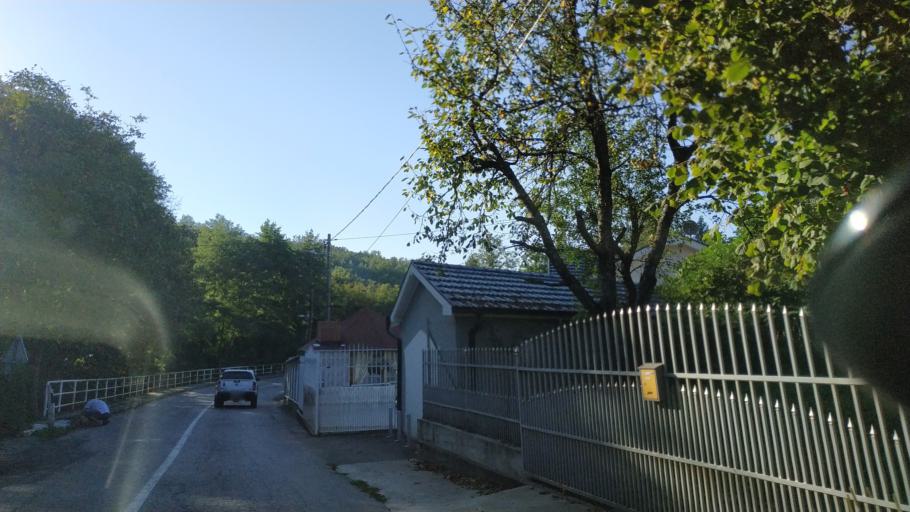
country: RS
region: Central Serbia
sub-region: Rasinski Okrug
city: Krusevac
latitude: 43.4710
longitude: 21.3557
